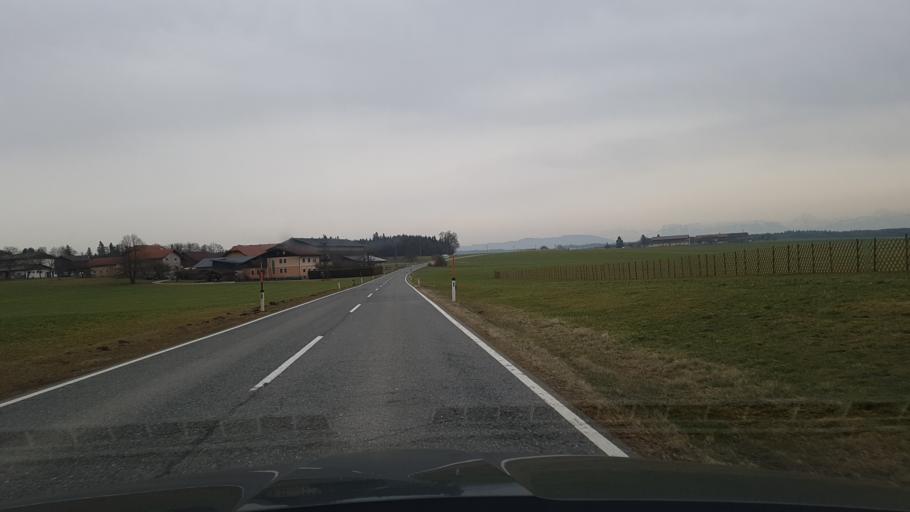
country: AT
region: Salzburg
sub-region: Politischer Bezirk Salzburg-Umgebung
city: Lamprechtshausen
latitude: 48.0280
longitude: 12.9566
